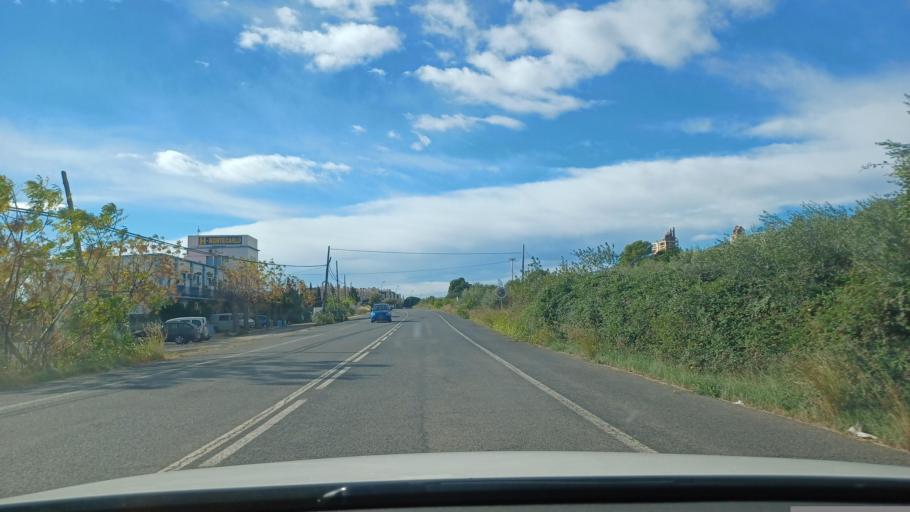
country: ES
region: Catalonia
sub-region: Provincia de Tarragona
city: Sant Carles de la Rapita
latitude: 40.5802
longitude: 0.5537
